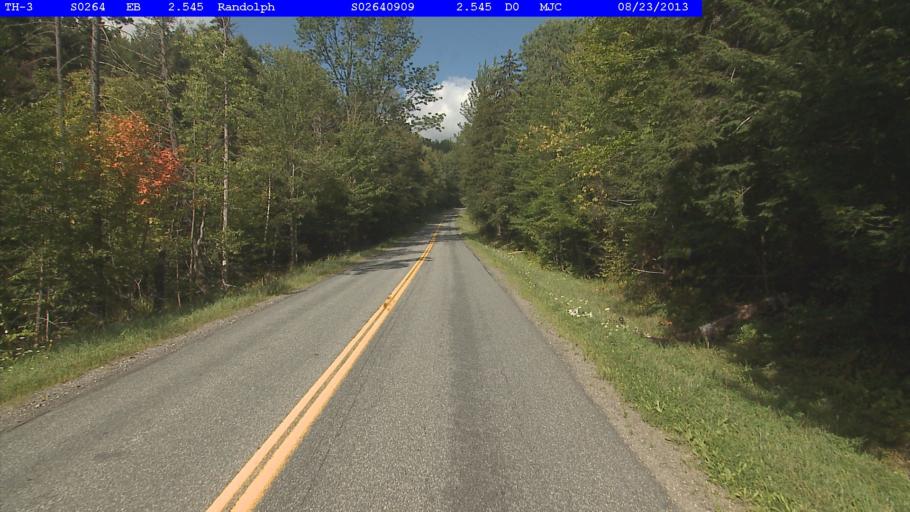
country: US
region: Vermont
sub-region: Orange County
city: Chelsea
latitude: 43.9621
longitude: -72.5275
